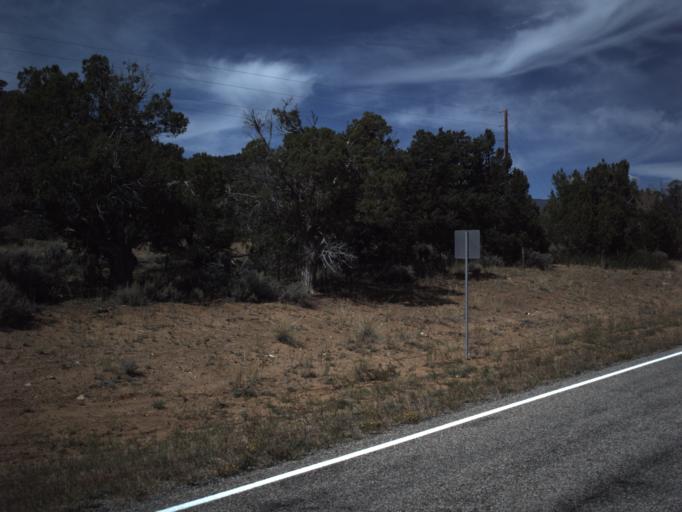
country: US
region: Utah
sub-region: Wayne County
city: Loa
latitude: 37.9183
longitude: -111.4247
